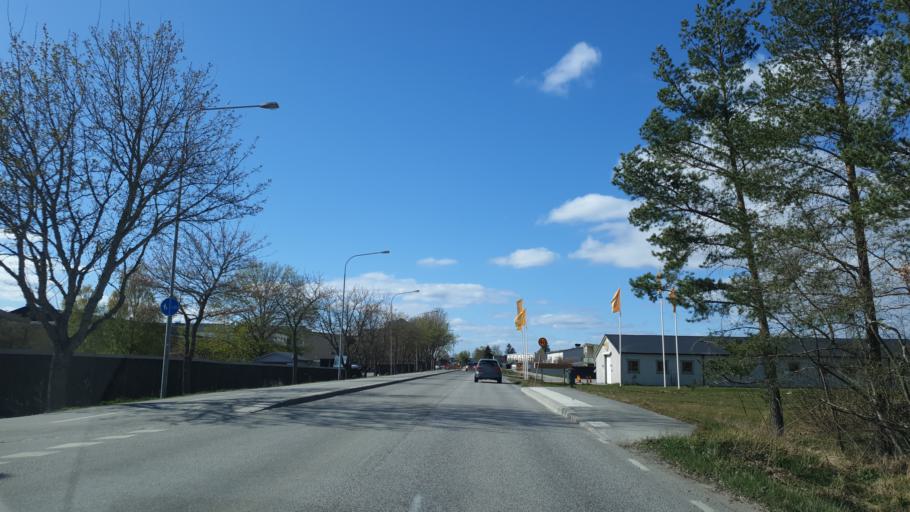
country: SE
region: Uppsala
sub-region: Uppsala Kommun
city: Gamla Uppsala
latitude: 59.8901
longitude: 17.6544
